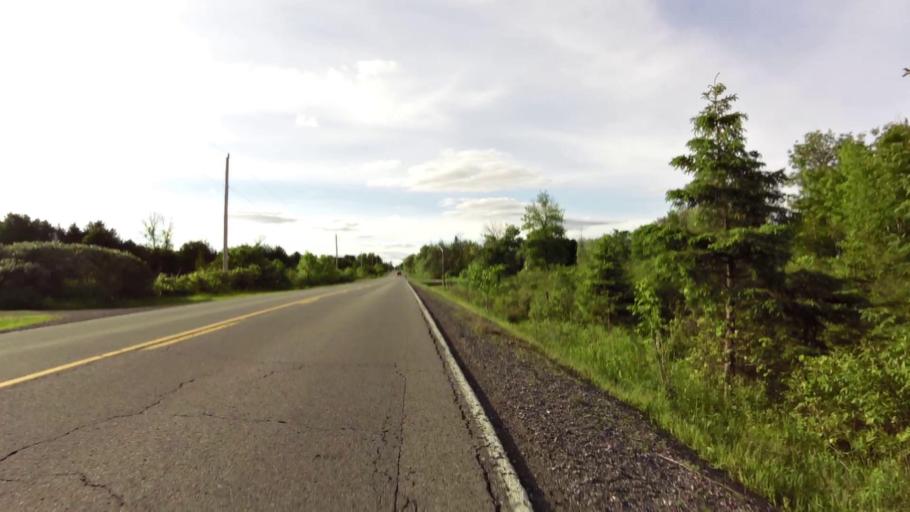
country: CA
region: Ontario
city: Ottawa
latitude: 45.2304
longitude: -75.6086
